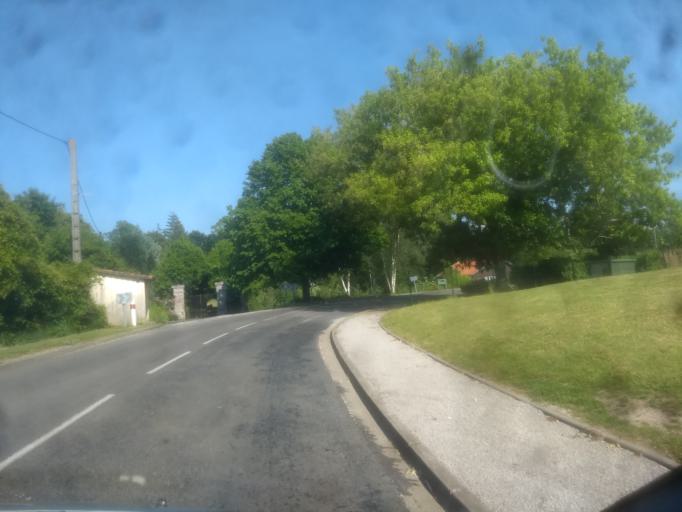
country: FR
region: Picardie
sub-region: Departement de la Somme
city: Crecy-en-Ponthieu
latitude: 50.1709
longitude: 1.8748
